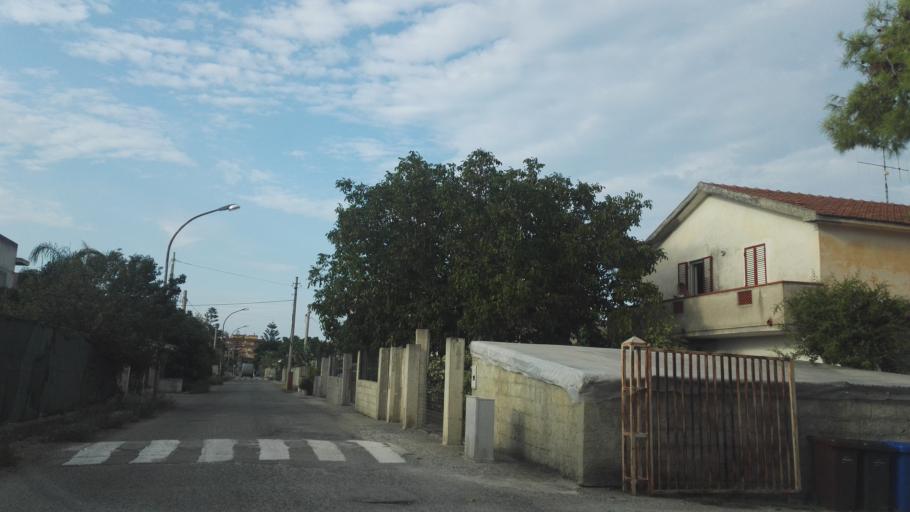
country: IT
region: Calabria
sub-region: Provincia di Reggio Calabria
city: Monasterace Marina
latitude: 38.4309
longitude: 16.5690
